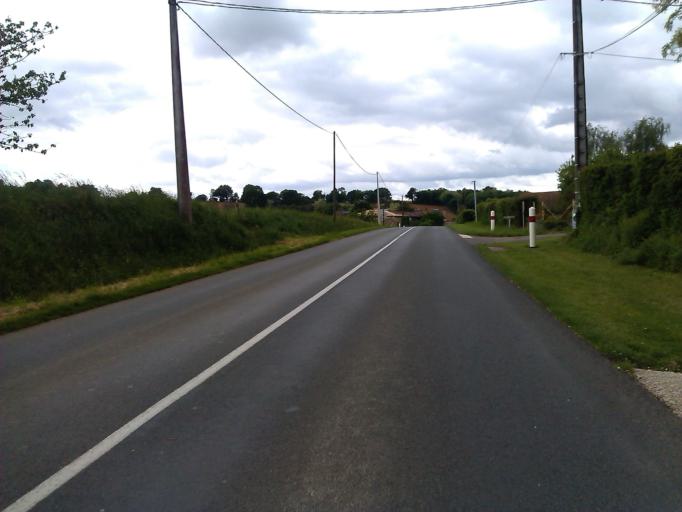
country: FR
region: Poitou-Charentes
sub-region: Departement de la Charente
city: Nanteuil-en-Vallee
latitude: 45.9848
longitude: 0.3558
